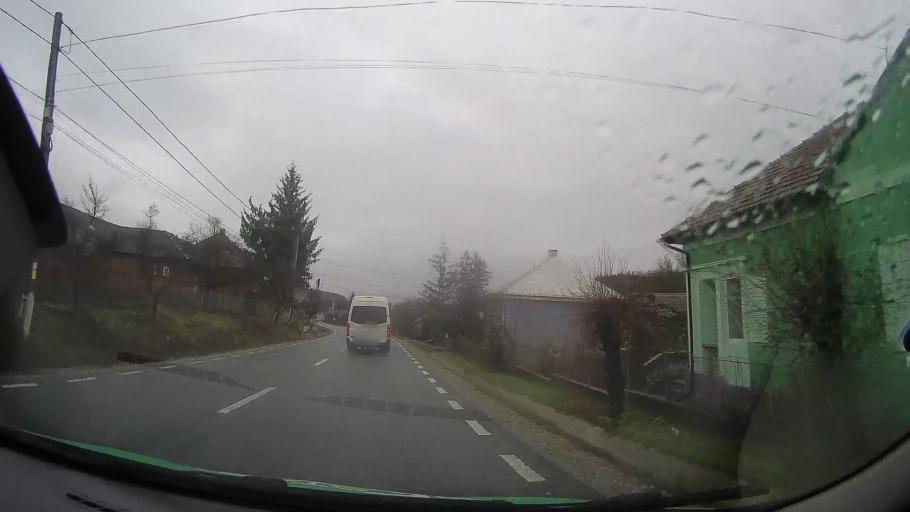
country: RO
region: Bistrita-Nasaud
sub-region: Comuna Galatii Bistritei
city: Galatii Bistritei
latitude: 47.0251
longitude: 24.4156
